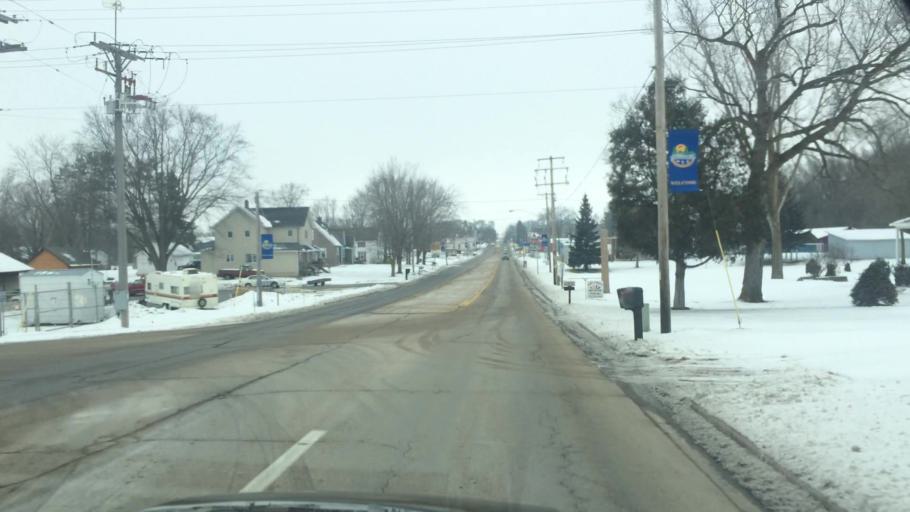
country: US
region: Wisconsin
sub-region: Shawano County
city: Bonduel
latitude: 44.7345
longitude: -88.4459
